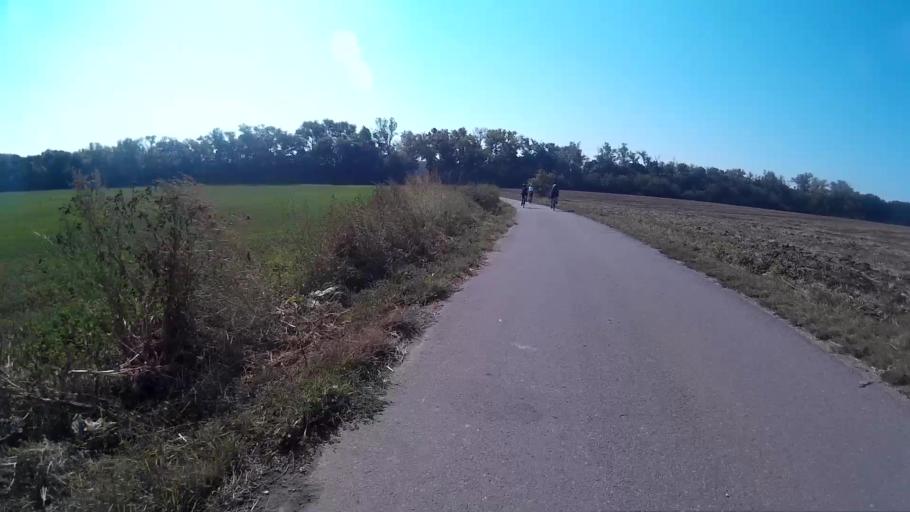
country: CZ
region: South Moravian
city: Drnholec
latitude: 48.8675
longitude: 16.5309
